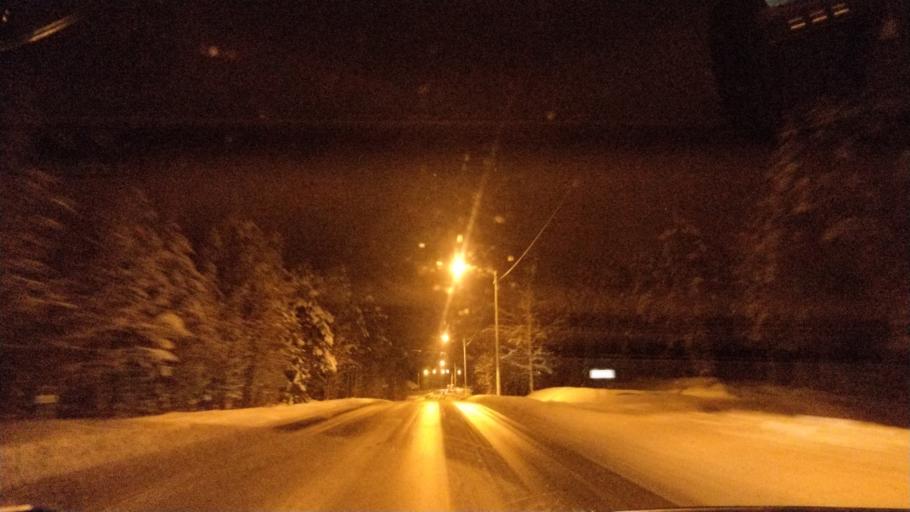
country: FI
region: Lapland
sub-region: Rovaniemi
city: Rovaniemi
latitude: 66.3201
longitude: 25.3590
